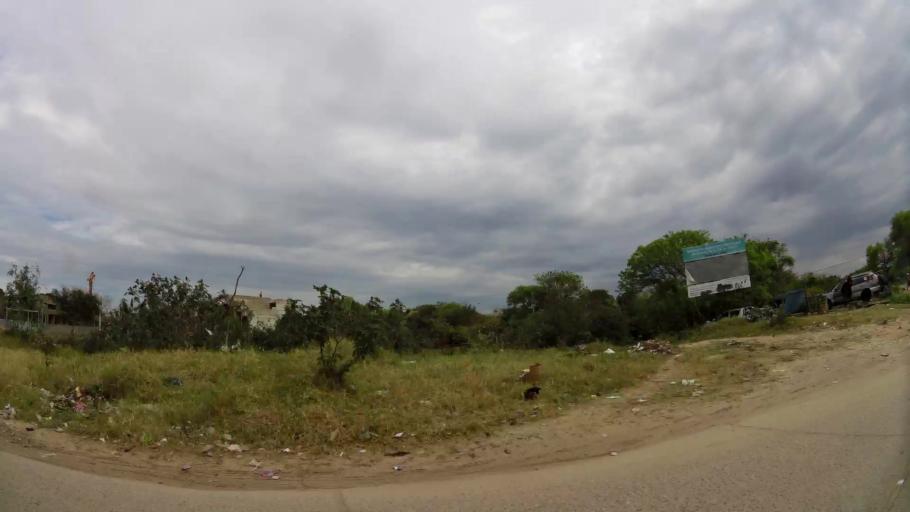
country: BO
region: Santa Cruz
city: Santa Cruz de la Sierra
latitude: -17.7452
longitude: -63.1947
